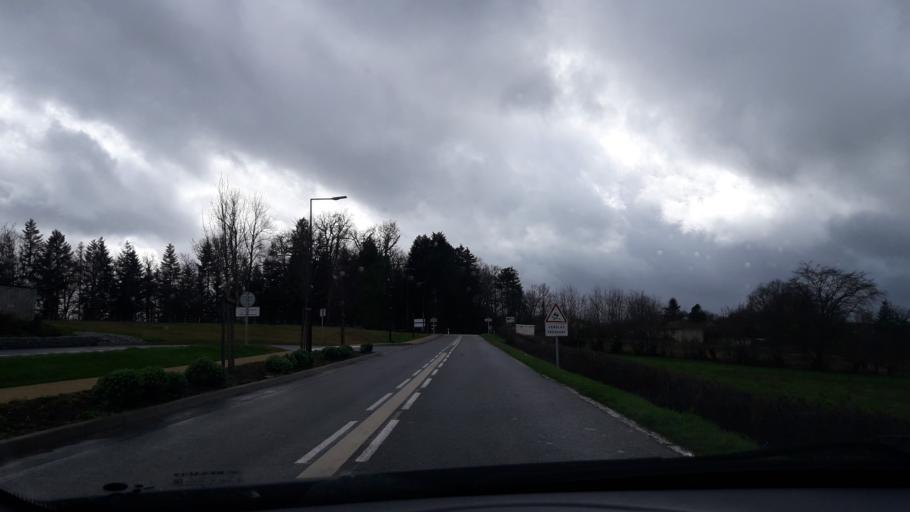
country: FR
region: Limousin
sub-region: Departement de la Haute-Vienne
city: Pierre-Buffiere
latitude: 45.7170
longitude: 1.3748
